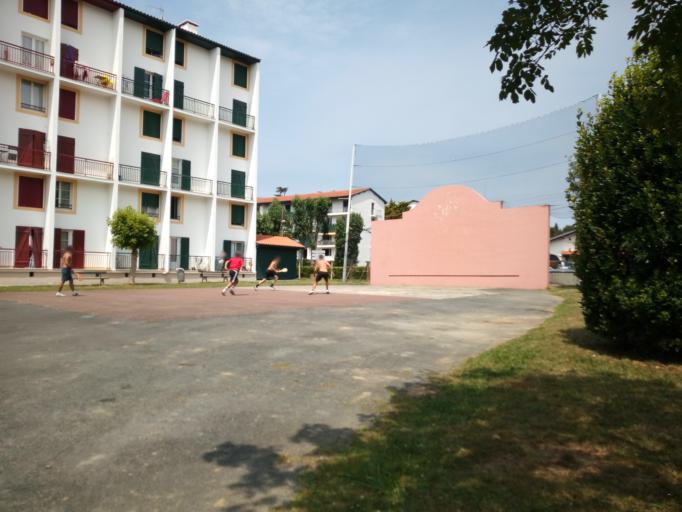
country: FR
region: Aquitaine
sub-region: Departement des Pyrenees-Atlantiques
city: Saint-Jean-de-Luz
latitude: 43.3984
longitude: -1.6560
